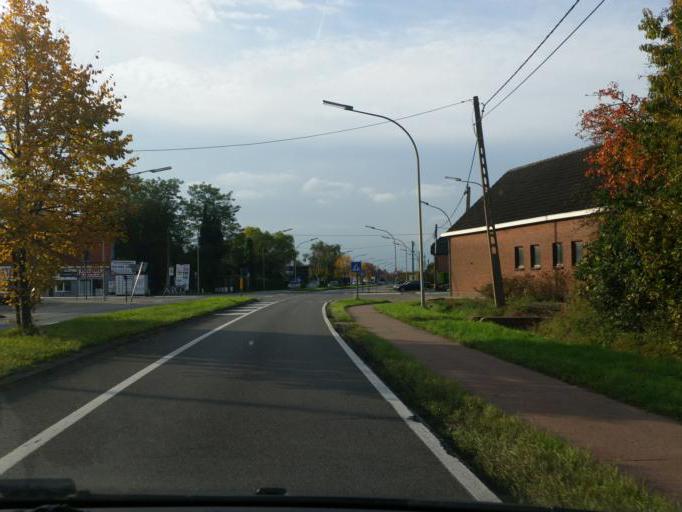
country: BE
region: Flanders
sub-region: Provincie Antwerpen
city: Berlaar
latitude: 51.0864
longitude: 4.6441
